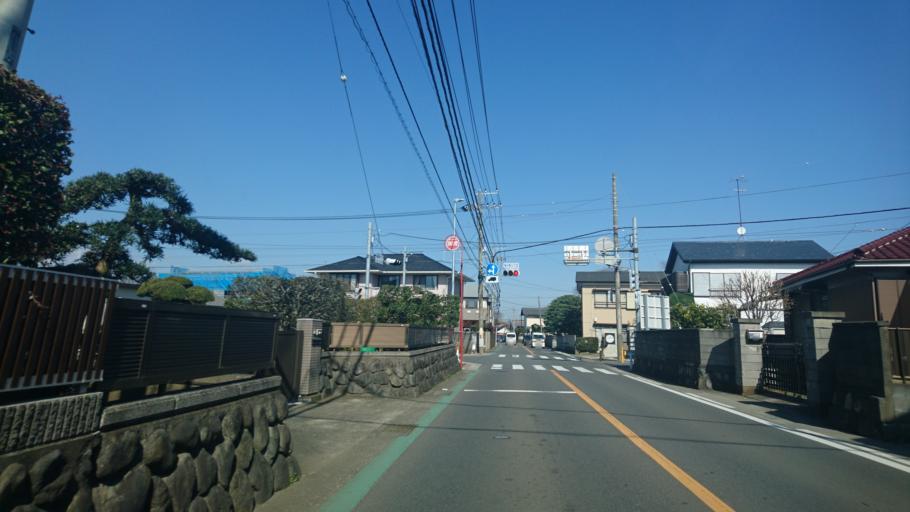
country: JP
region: Kanagawa
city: Fujisawa
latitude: 35.3847
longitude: 139.4786
